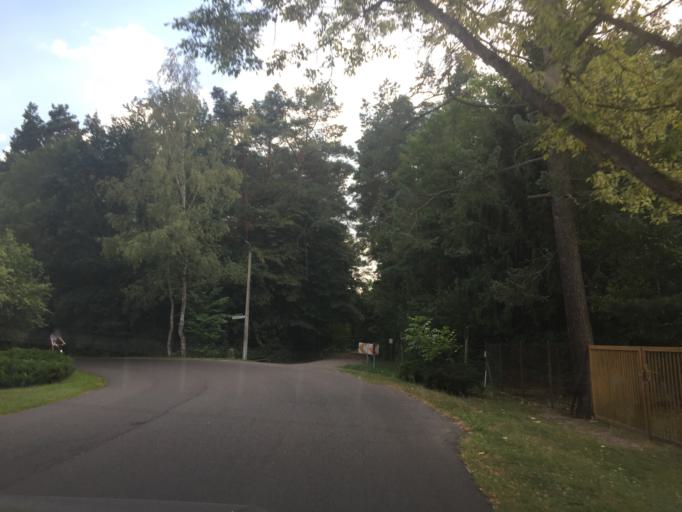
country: DE
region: Brandenburg
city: Erkner
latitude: 52.3810
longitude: 13.7688
